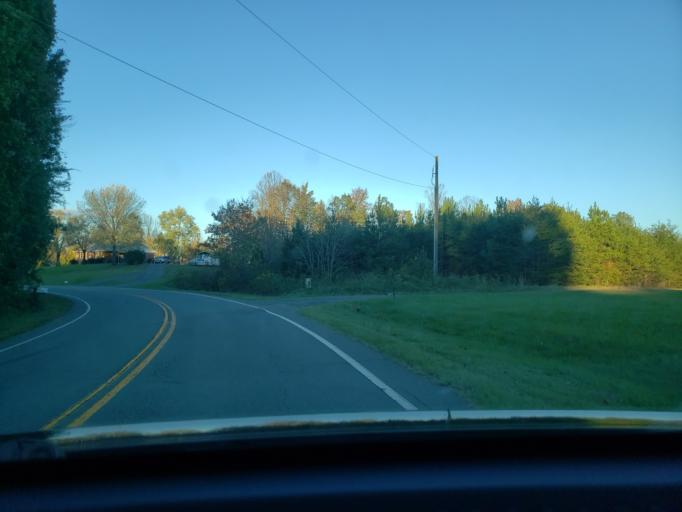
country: US
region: North Carolina
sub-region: Forsyth County
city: Rural Hall
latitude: 36.3153
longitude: -80.2366
